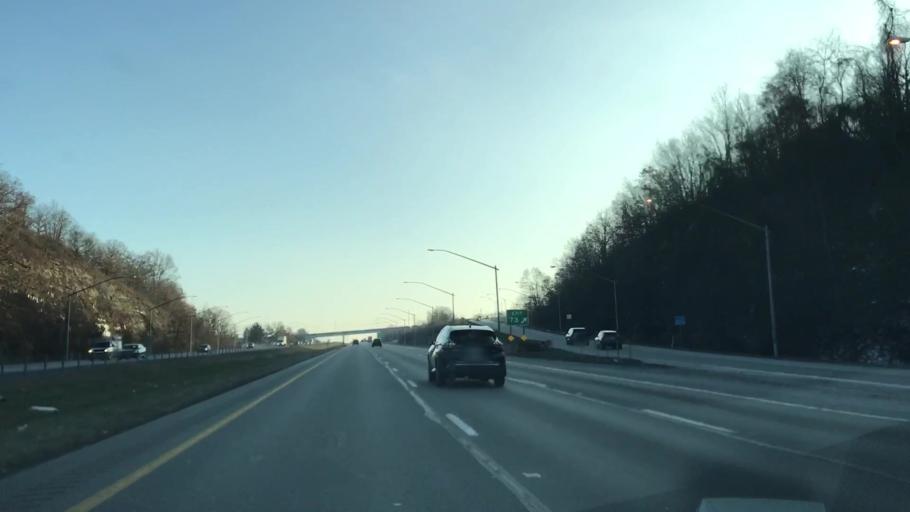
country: US
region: Pennsylvania
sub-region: Allegheny County
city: Bradford Woods
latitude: 40.6215
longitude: -80.0964
